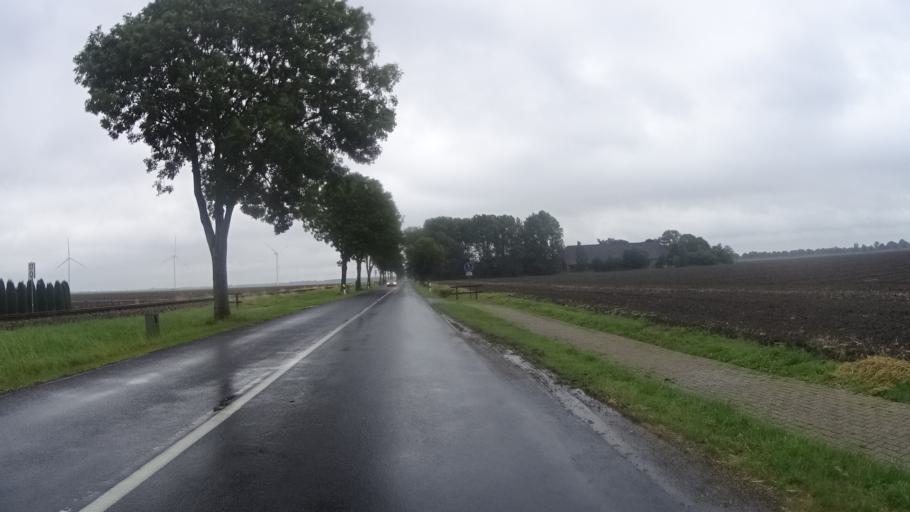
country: DE
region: Lower Saxony
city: Bunde
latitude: 53.1881
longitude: 7.2173
